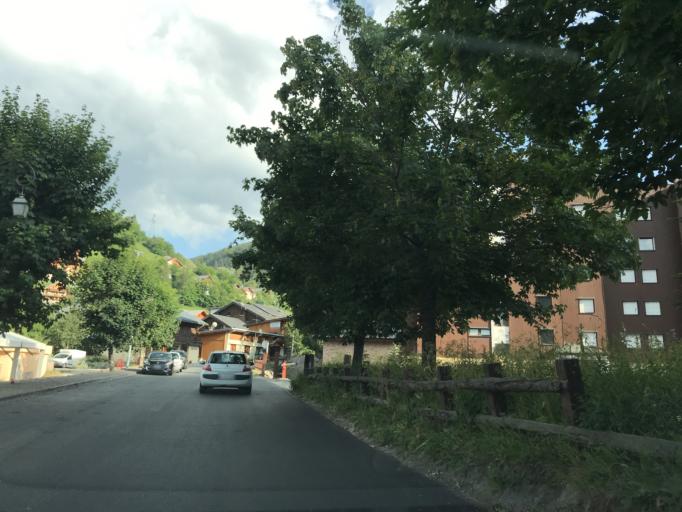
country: FR
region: Rhone-Alpes
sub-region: Departement de la Savoie
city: Valloire
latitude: 45.1674
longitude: 6.4302
